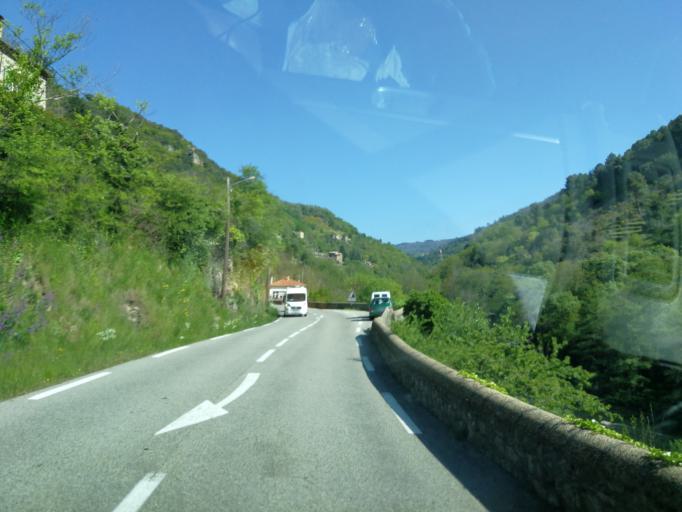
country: FR
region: Rhone-Alpes
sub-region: Departement de l'Ardeche
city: Saint-Sauveur-de-Montagut
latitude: 44.8271
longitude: 4.5767
